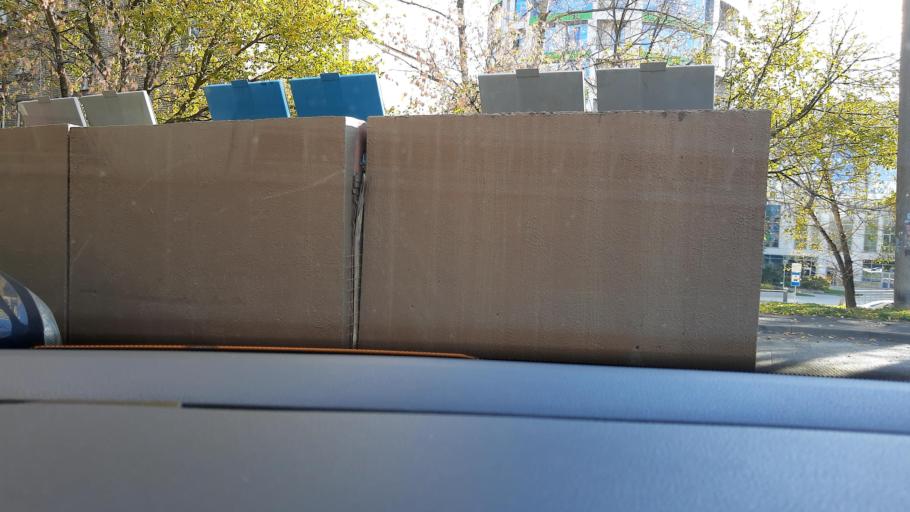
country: RU
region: Moscow
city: Vorob'yovo
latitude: 55.7368
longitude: 37.5307
